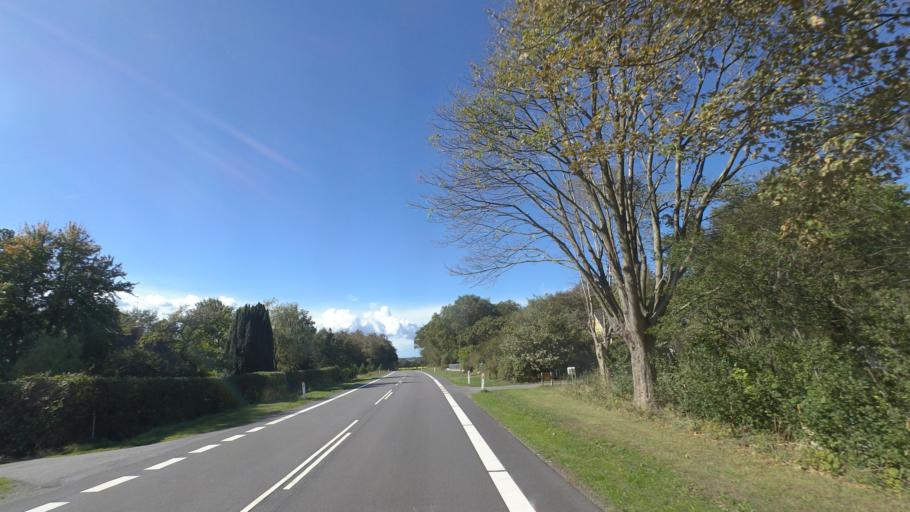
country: DK
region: Capital Region
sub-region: Bornholm Kommune
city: Akirkeby
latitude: 55.0681
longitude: 14.9947
